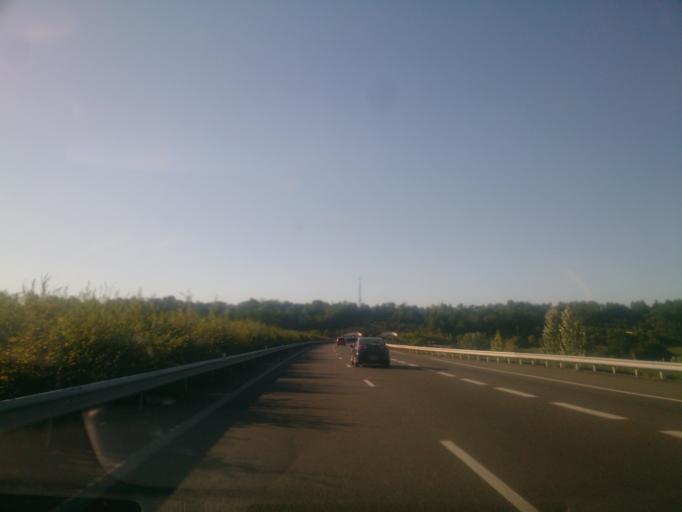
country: FR
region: Midi-Pyrenees
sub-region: Departement du Tarn-et-Garonne
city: Caussade
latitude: 44.2465
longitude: 1.5142
